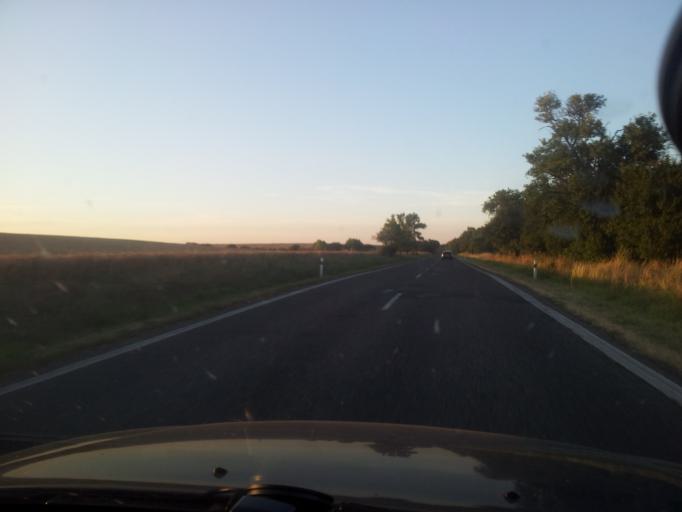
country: SK
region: Nitriansky
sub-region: Okres Nove Zamky
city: Sturovo
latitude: 47.8719
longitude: 18.6371
